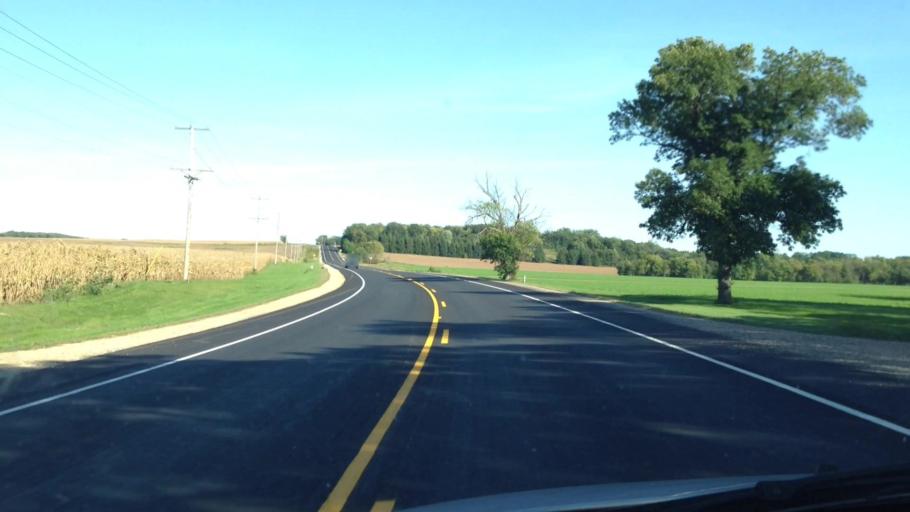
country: US
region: Minnesota
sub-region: Washington County
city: Oak Park Heights
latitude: 45.0420
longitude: -92.7740
